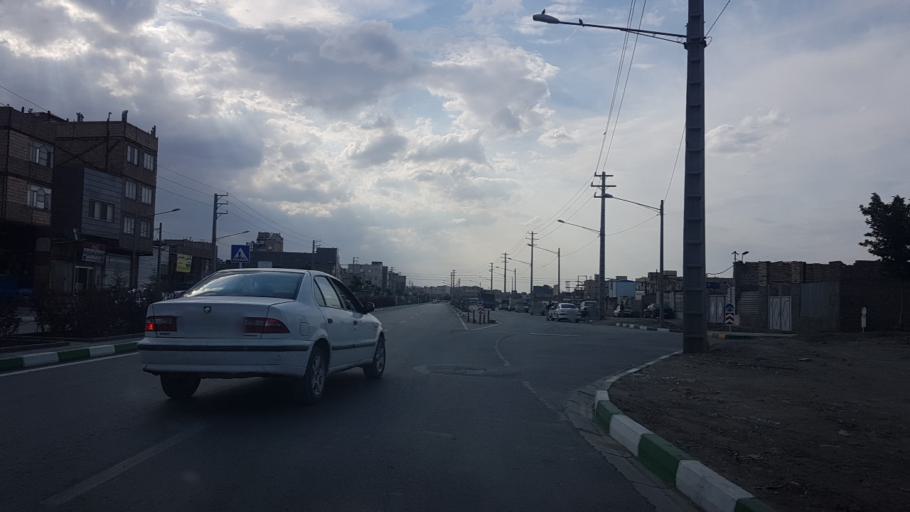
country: IR
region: Razavi Khorasan
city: Mashhad
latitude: 36.3545
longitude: 59.5692
